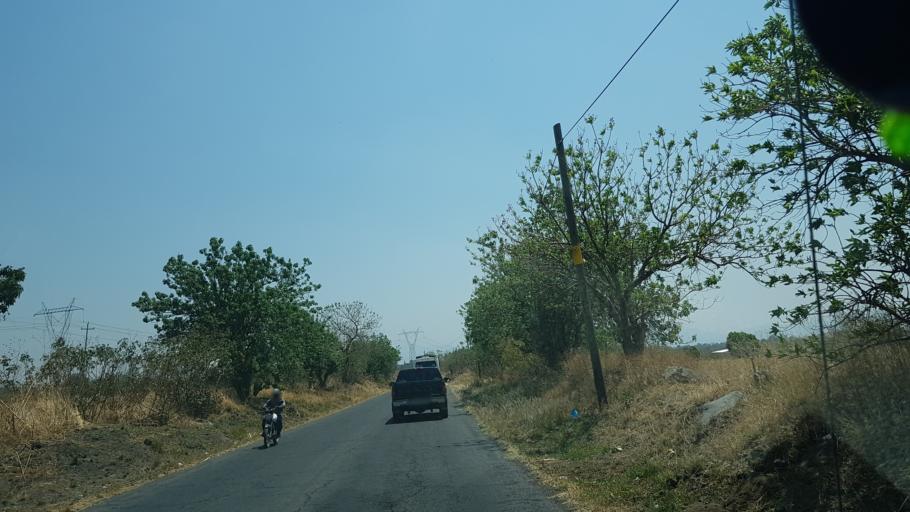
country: MX
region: Puebla
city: Tochimilco
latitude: 18.8889
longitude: -98.5292
